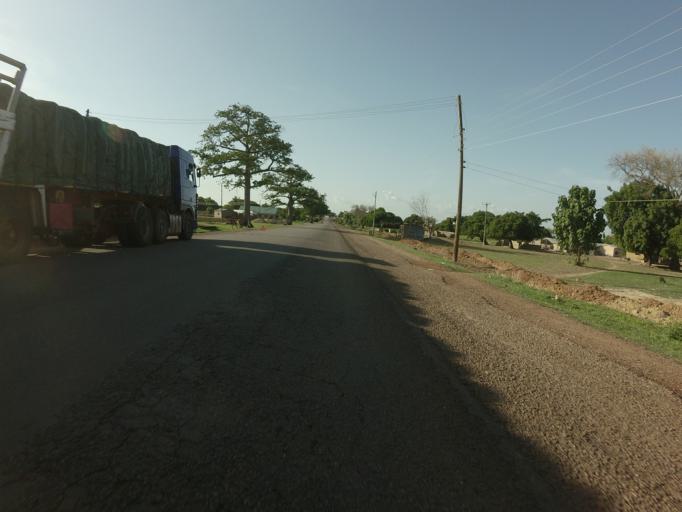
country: GH
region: Upper East
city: Navrongo
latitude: 10.9130
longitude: -1.0900
